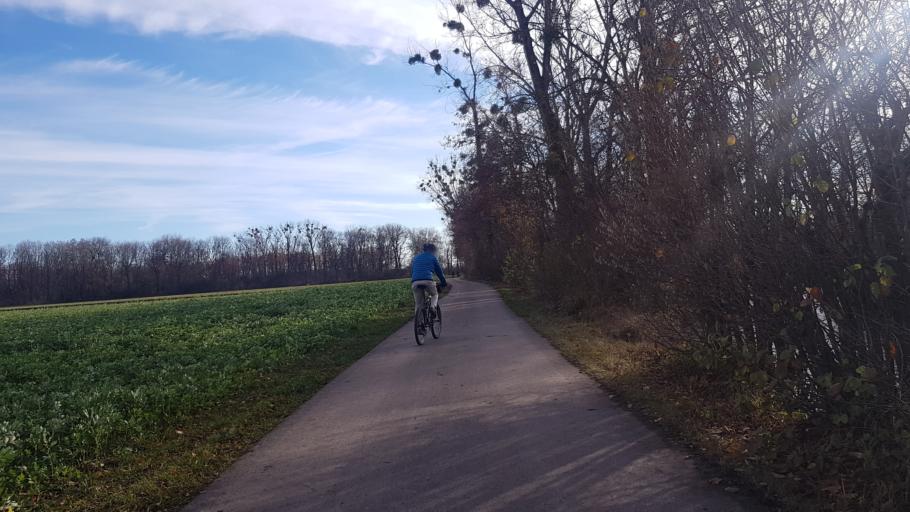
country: DE
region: Bavaria
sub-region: Upper Bavaria
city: Oberschleissheim
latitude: 48.2350
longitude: 11.5285
